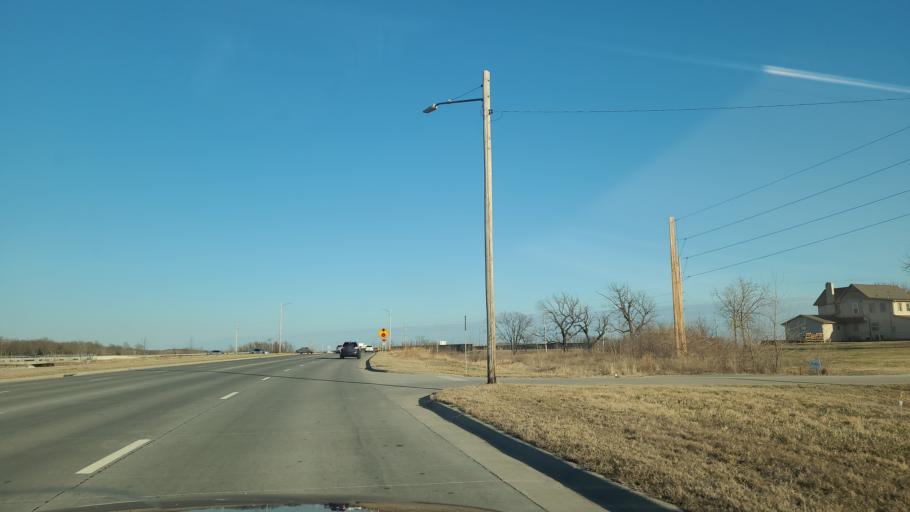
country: US
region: Kansas
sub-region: Douglas County
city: Lawrence
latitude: 38.9281
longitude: -95.2443
